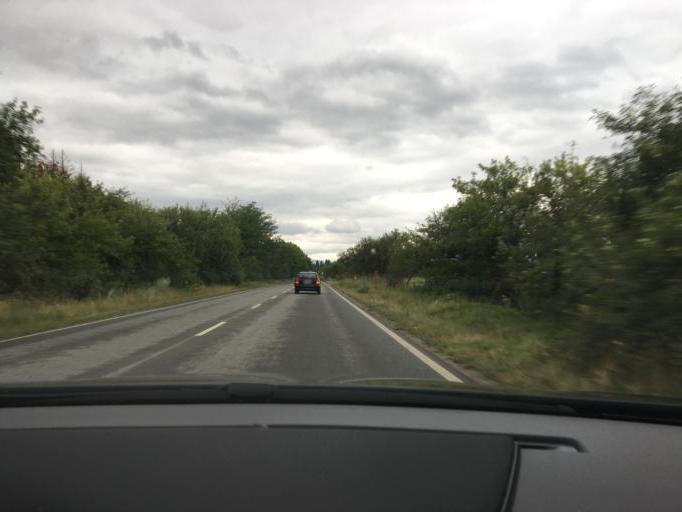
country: BG
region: Kyustendil
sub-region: Obshtina Kyustendil
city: Kyustendil
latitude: 42.2585
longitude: 22.8380
